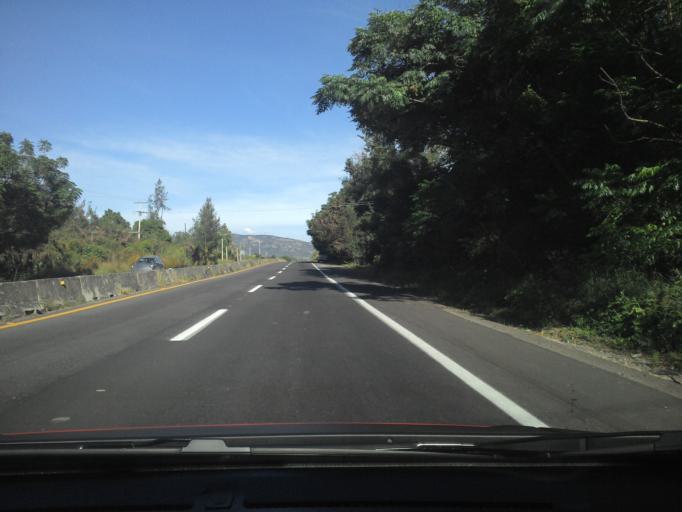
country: MX
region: Jalisco
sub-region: Tala
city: Los Ruisenores
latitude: 20.7179
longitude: -103.6356
